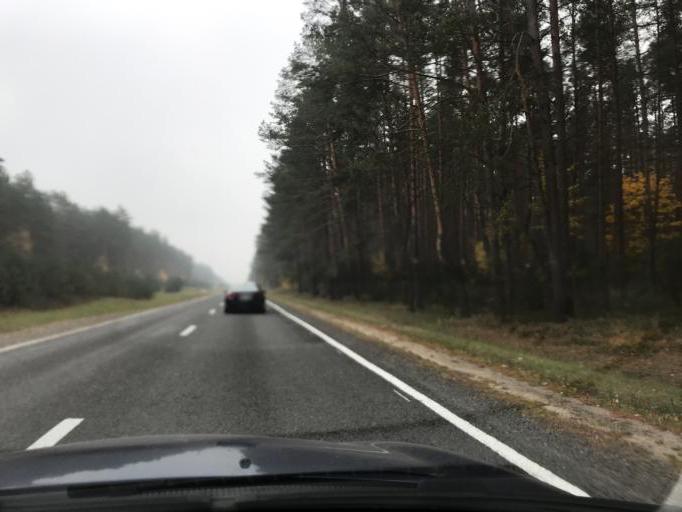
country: LT
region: Alytaus apskritis
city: Druskininkai
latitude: 53.8667
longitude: 23.8939
